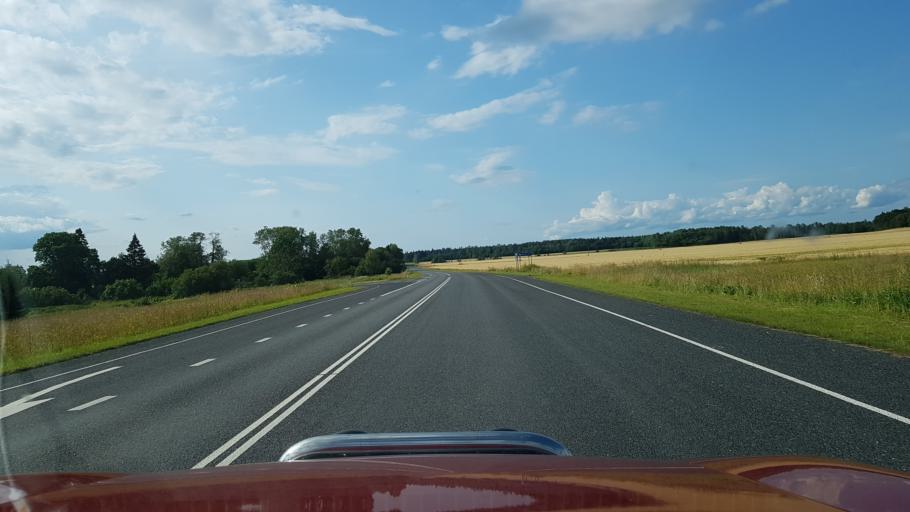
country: EE
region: Jaervamaa
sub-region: Jaerva-Jaani vald
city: Jarva-Jaani
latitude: 59.1156
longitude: 25.7936
